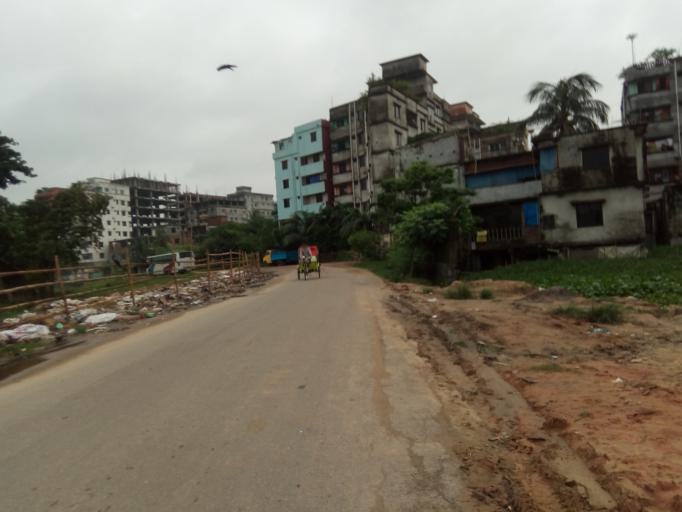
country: BD
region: Dhaka
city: Tungi
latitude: 23.8504
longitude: 90.4157
